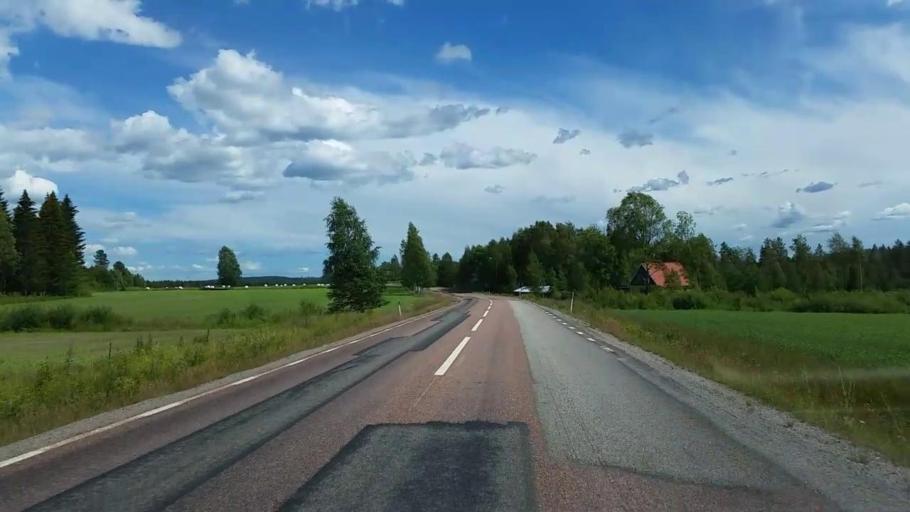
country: SE
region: Gaevleborg
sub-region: Ovanakers Kommun
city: Edsbyn
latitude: 61.3461
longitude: 15.6253
